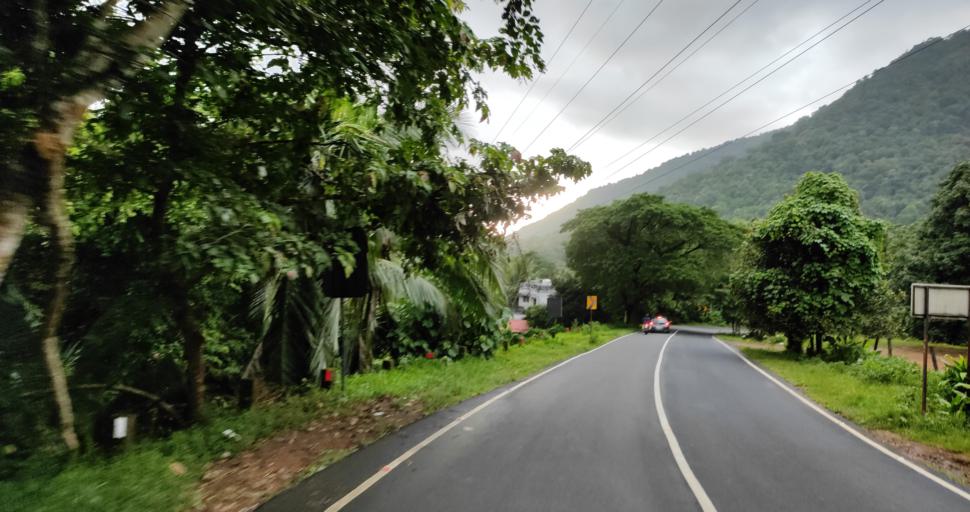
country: IN
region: Kerala
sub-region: Ernakulam
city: Angamali
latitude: 10.2989
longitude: 76.4499
